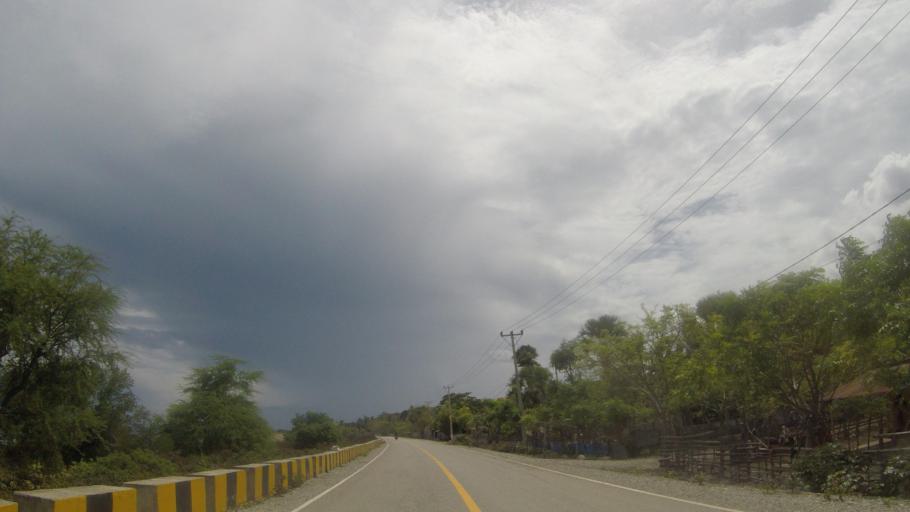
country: TL
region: Baucau
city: Baucau
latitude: -8.4511
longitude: 126.6379
